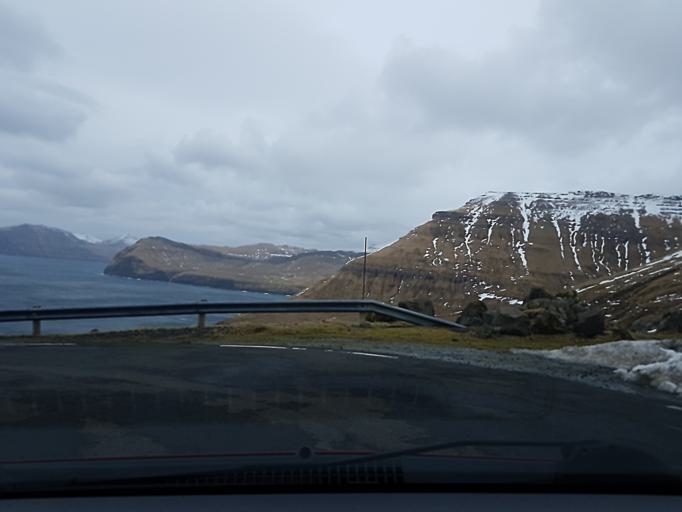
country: FO
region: Streymoy
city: Kollafjordhur
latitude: 62.0175
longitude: -6.9041
